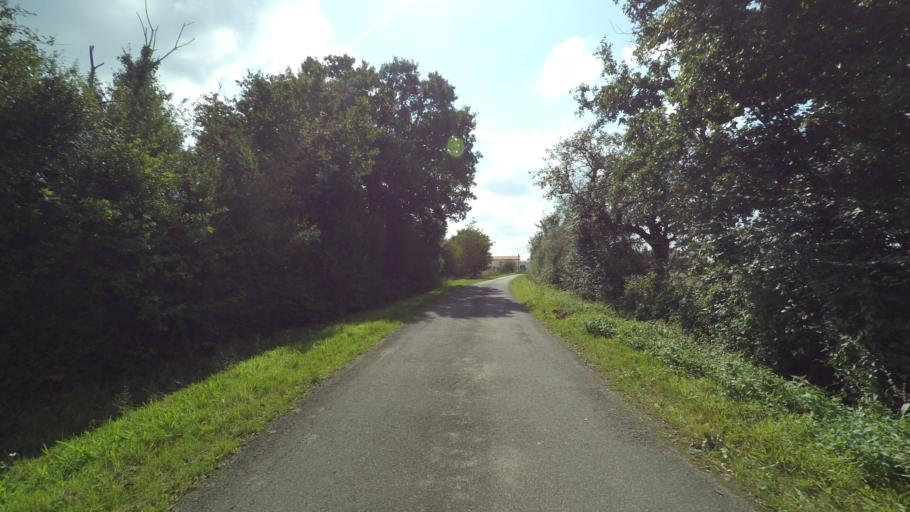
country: FR
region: Pays de la Loire
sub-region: Departement de la Loire-Atlantique
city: Vieillevigne
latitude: 46.9674
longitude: -1.4082
